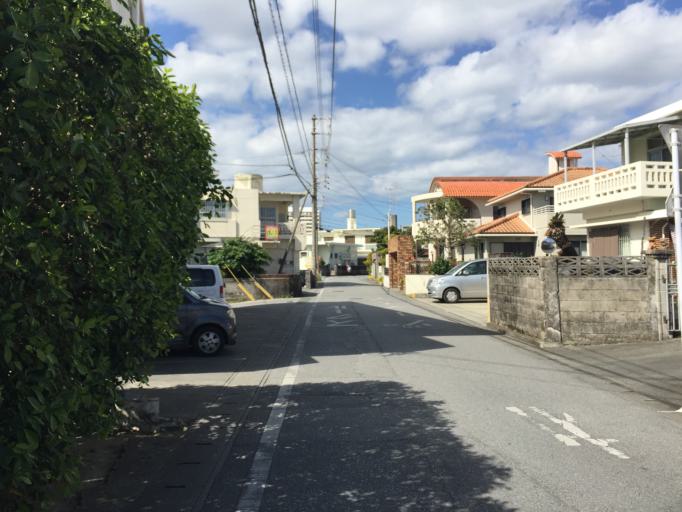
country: JP
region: Okinawa
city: Ginowan
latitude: 26.2337
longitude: 127.7343
